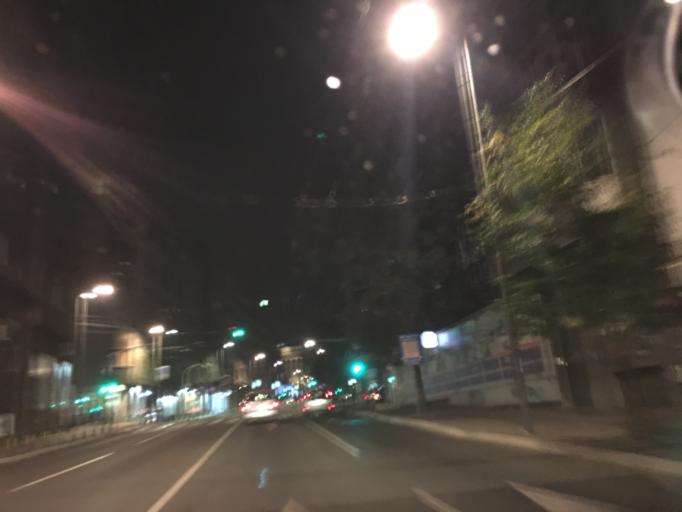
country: RS
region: Central Serbia
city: Belgrade
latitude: 44.8127
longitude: 20.4711
